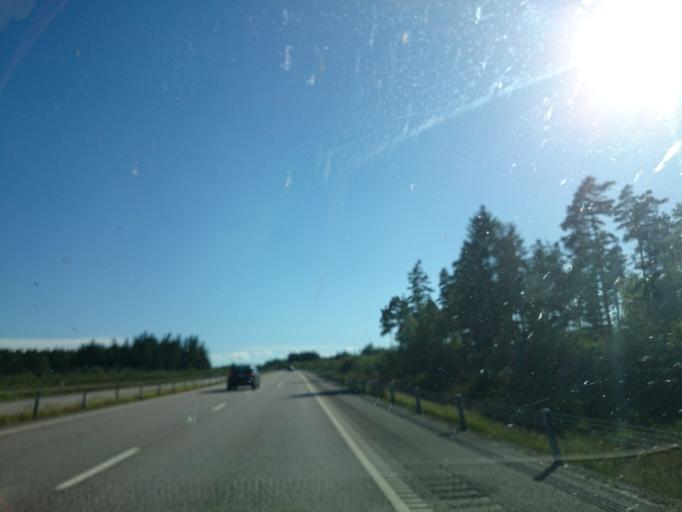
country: SE
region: Kronoberg
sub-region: Markaryds Kommun
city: Markaryd
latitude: 56.4304
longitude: 13.5670
